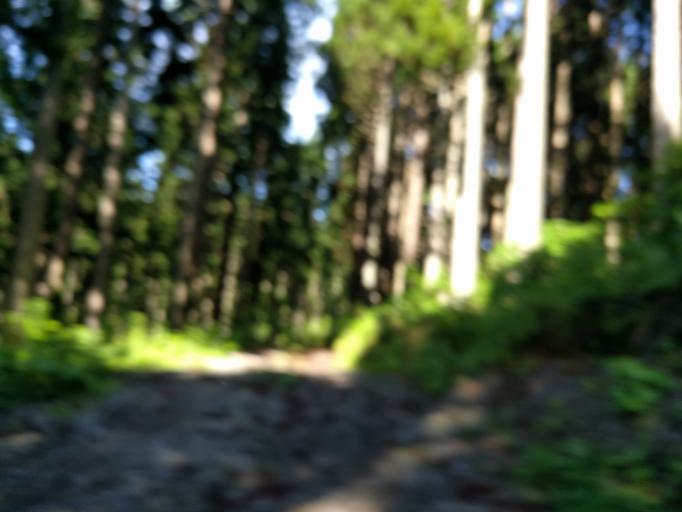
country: JP
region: Fukushima
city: Kitakata
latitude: 37.3832
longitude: 139.8239
